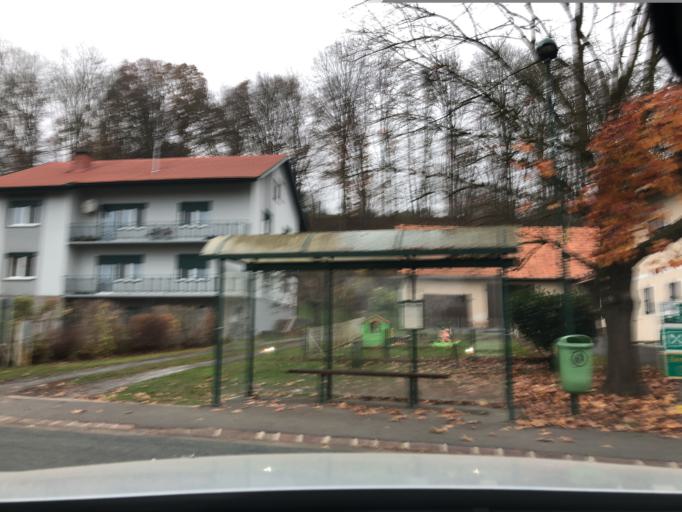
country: AT
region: Styria
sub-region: Politischer Bezirk Suedoststeiermark
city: Fehring
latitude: 46.9556
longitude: 16.0364
